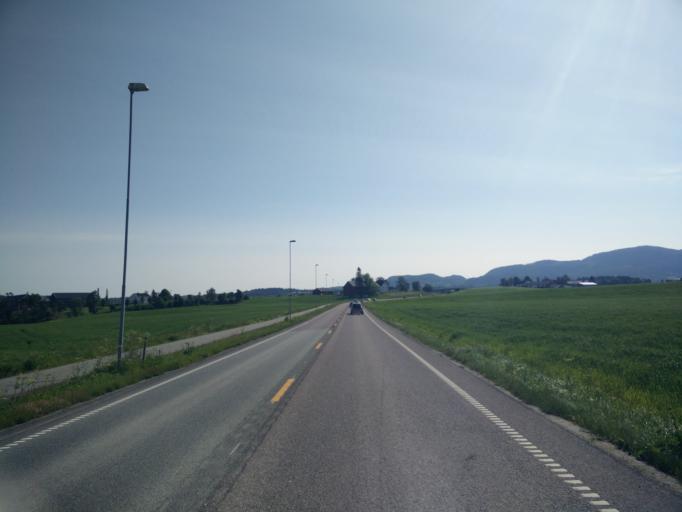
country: NO
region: Sor-Trondelag
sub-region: Melhus
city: Melhus
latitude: 63.3244
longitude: 10.2821
